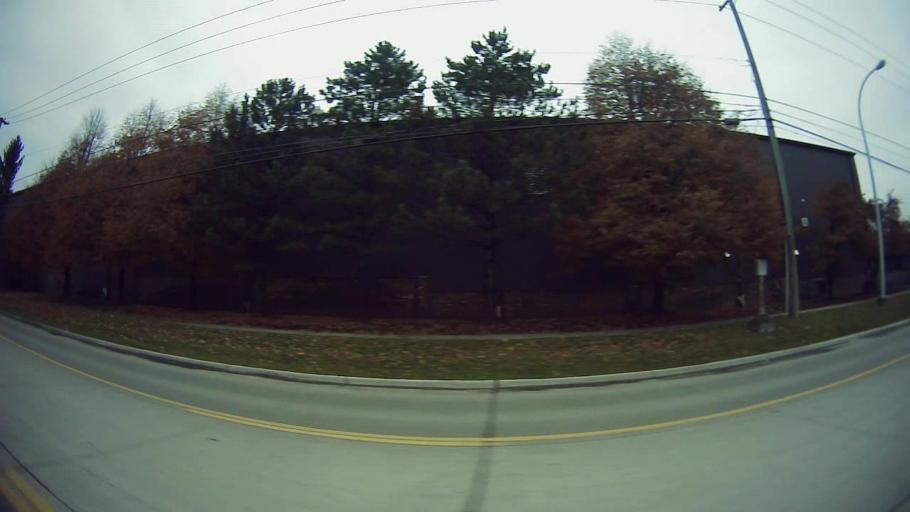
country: US
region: Michigan
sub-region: Oakland County
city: Southfield
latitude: 42.4450
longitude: -83.2395
